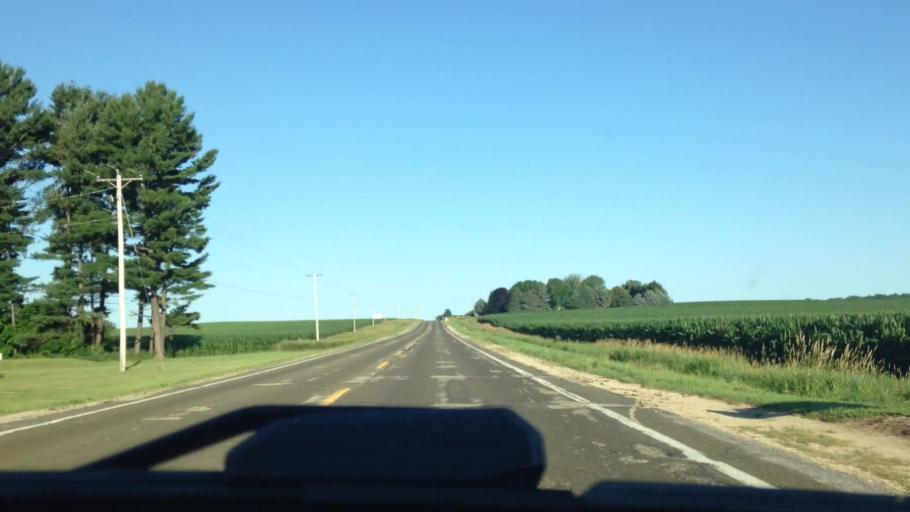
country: US
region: Wisconsin
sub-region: Columbia County
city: Poynette
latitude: 43.3378
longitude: -89.4088
